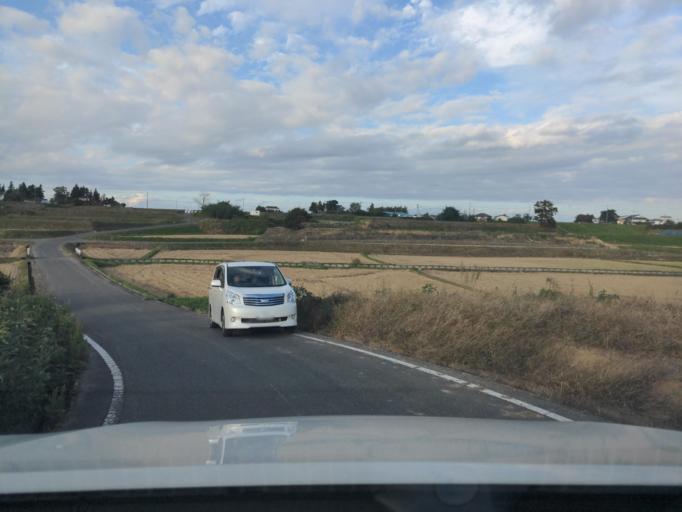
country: JP
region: Fukushima
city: Koriyama
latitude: 37.4363
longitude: 140.3653
